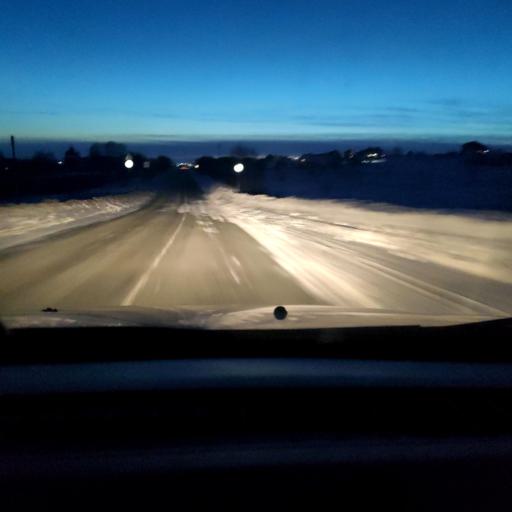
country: RU
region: Samara
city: Kinel'
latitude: 53.2728
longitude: 50.6113
